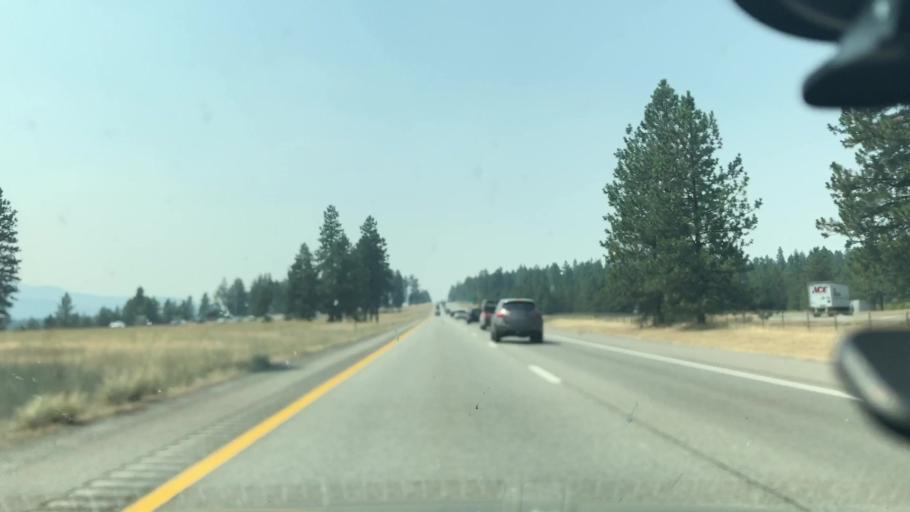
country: US
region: Idaho
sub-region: Kootenai County
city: Post Falls
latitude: 47.7093
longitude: -116.8659
